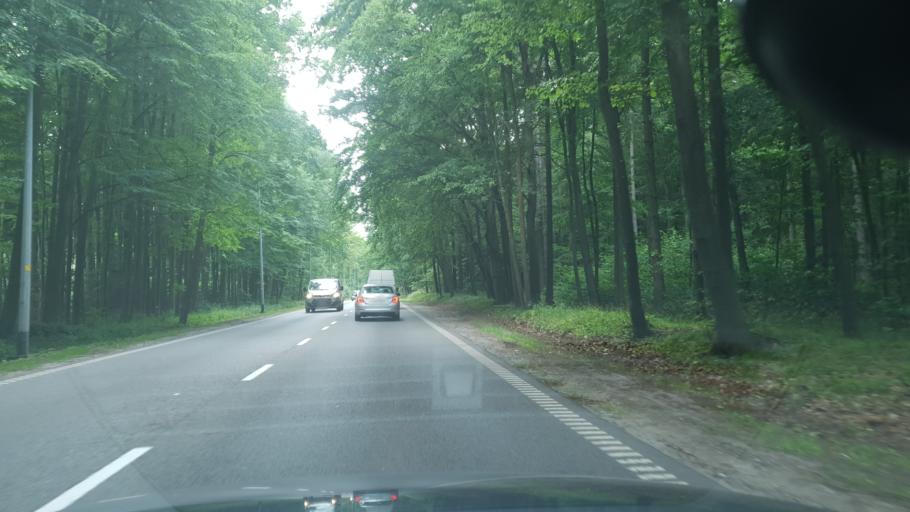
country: PL
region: Pomeranian Voivodeship
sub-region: Gdynia
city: Wielki Kack
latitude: 54.4221
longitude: 18.5118
